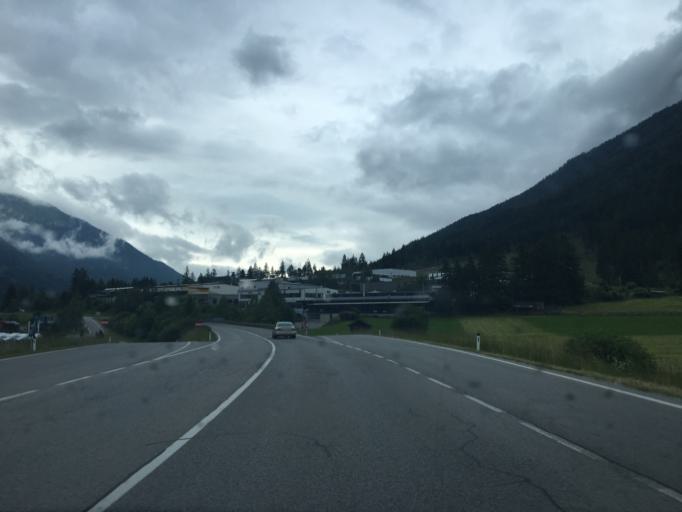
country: AT
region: Tyrol
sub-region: Politischer Bezirk Innsbruck Land
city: Neustift im Stubaital
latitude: 47.1314
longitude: 11.3402
